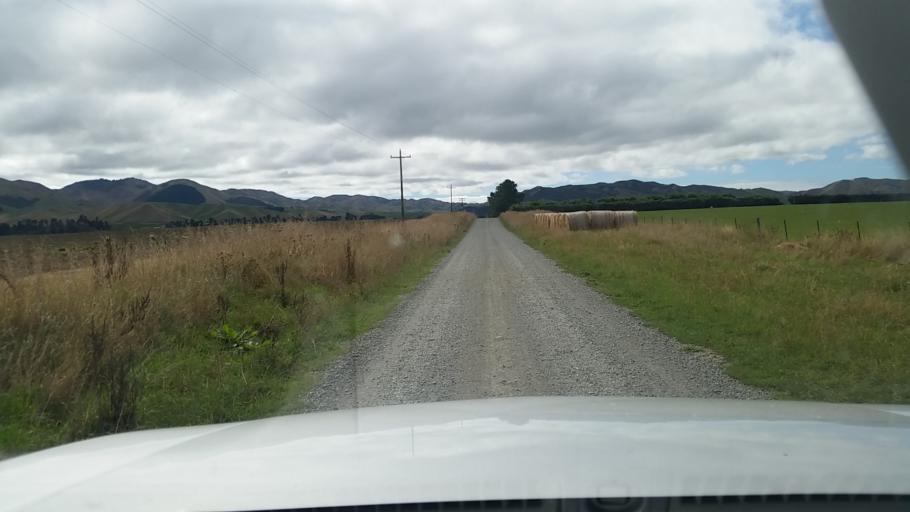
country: NZ
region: Marlborough
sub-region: Marlborough District
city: Blenheim
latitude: -41.6800
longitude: 174.0387
